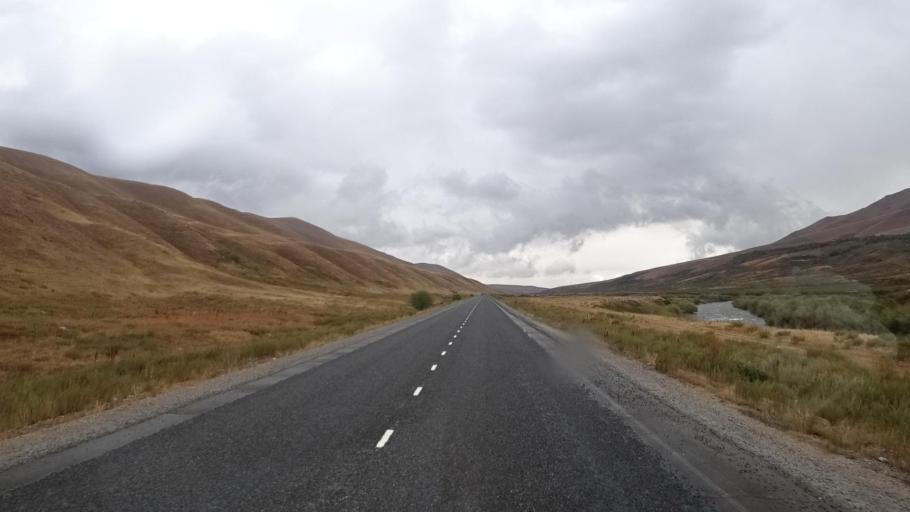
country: KG
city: Sosnovka
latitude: 42.1990
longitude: 73.5760
